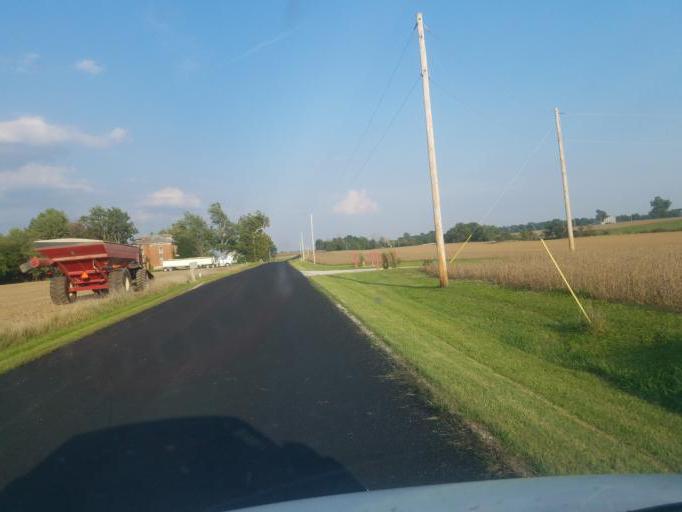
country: US
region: Ohio
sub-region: Crawford County
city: Bucyrus
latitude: 40.9661
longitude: -83.0047
